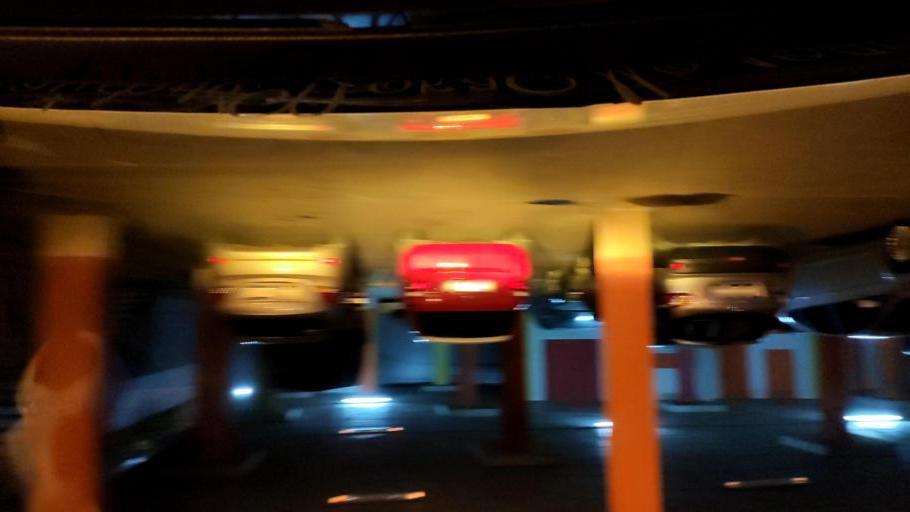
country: RU
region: Voronezj
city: Podgornoye
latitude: 51.6946
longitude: 39.1435
